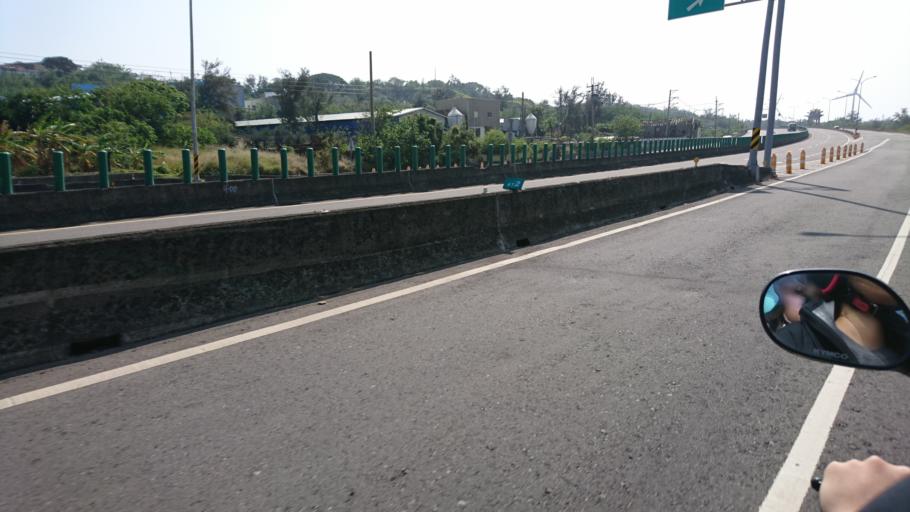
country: TW
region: Taiwan
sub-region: Hsinchu
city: Hsinchu
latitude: 24.7257
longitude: 120.8708
